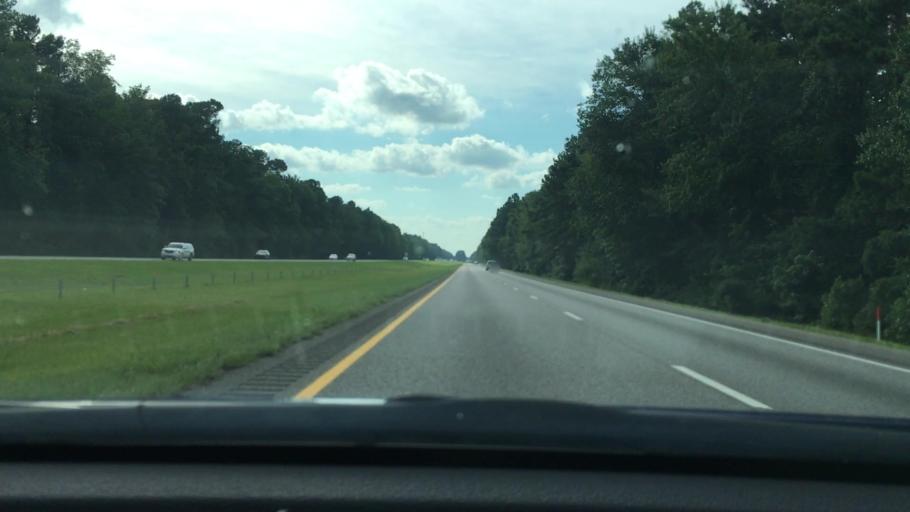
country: US
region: South Carolina
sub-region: Dorchester County
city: Ridgeville
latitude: 33.1300
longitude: -80.2953
